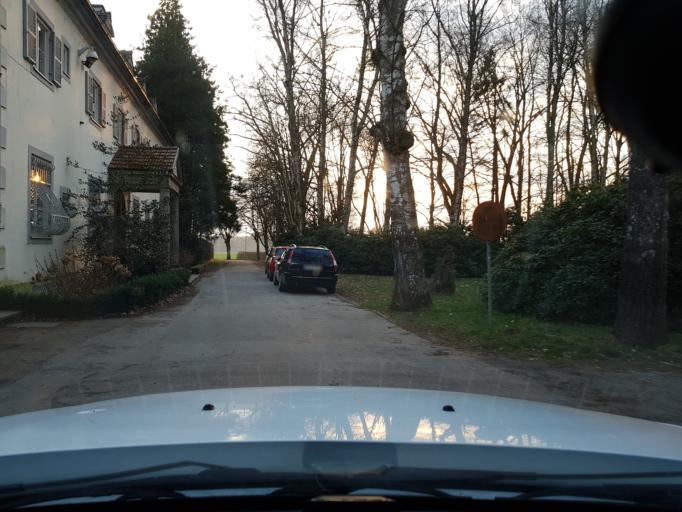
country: PL
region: West Pomeranian Voivodeship
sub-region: Koszalin
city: Koszalin
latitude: 54.1042
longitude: 16.1613
